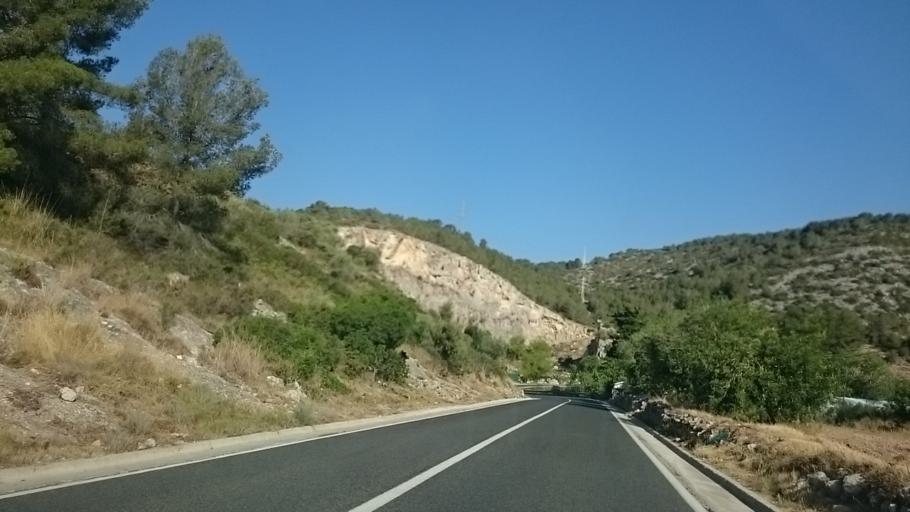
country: ES
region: Catalonia
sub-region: Provincia de Barcelona
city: Sant Pere de Ribes
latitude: 41.2675
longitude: 1.7675
